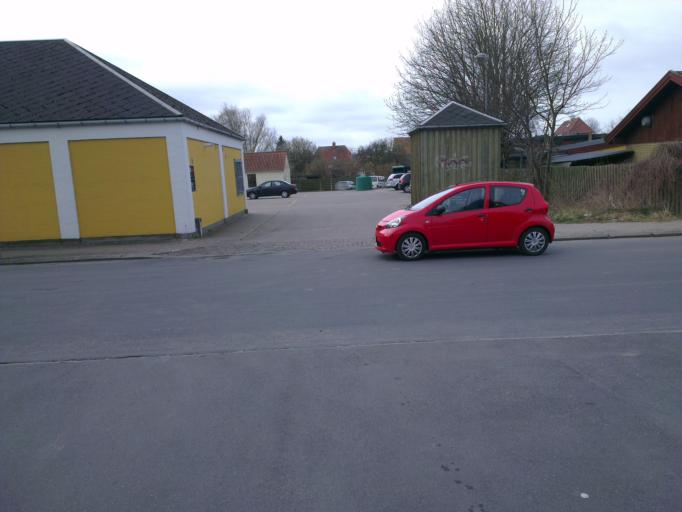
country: PL
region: Lower Silesian Voivodeship
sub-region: Powiat olesnicki
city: Dziadowa Kloda
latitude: 51.2390
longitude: 17.7235
